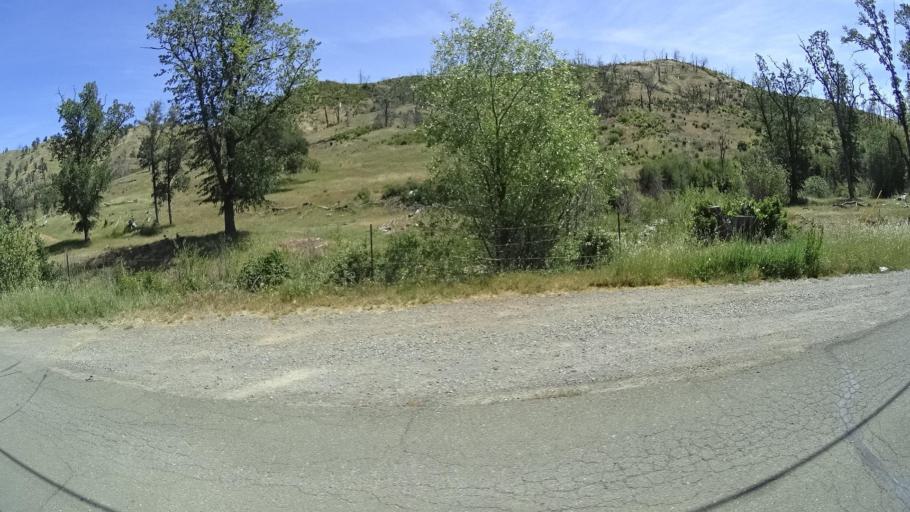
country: US
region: California
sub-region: Lake County
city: Middletown
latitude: 38.7771
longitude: -122.6294
